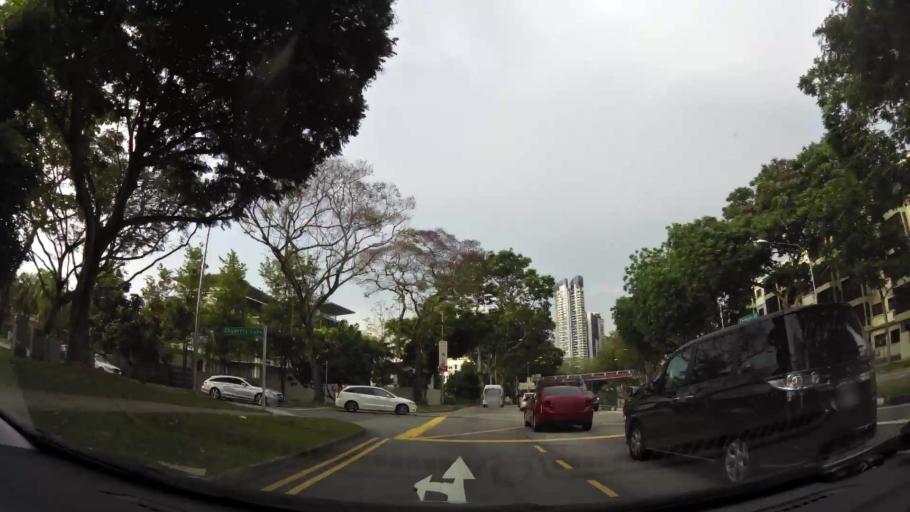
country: SG
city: Singapore
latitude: 1.3221
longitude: 103.8415
